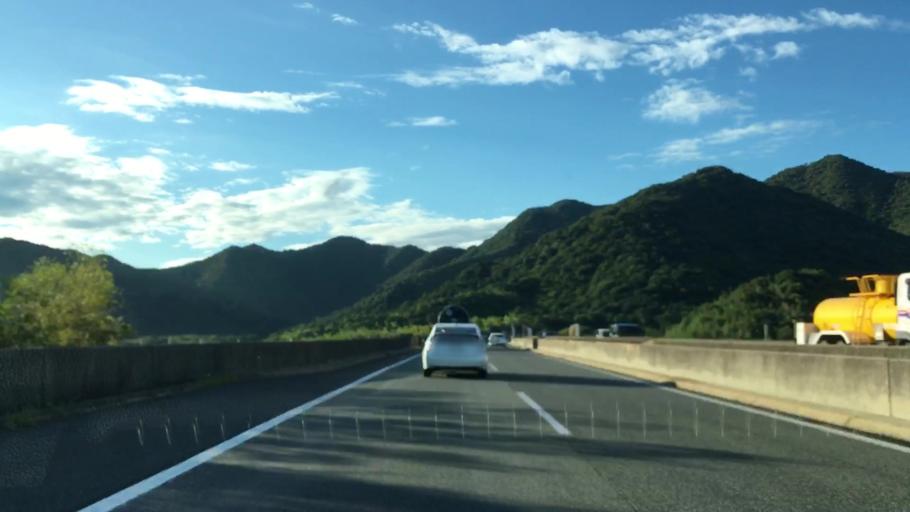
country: JP
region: Yamaguchi
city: Ogori-shimogo
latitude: 34.0956
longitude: 131.4538
